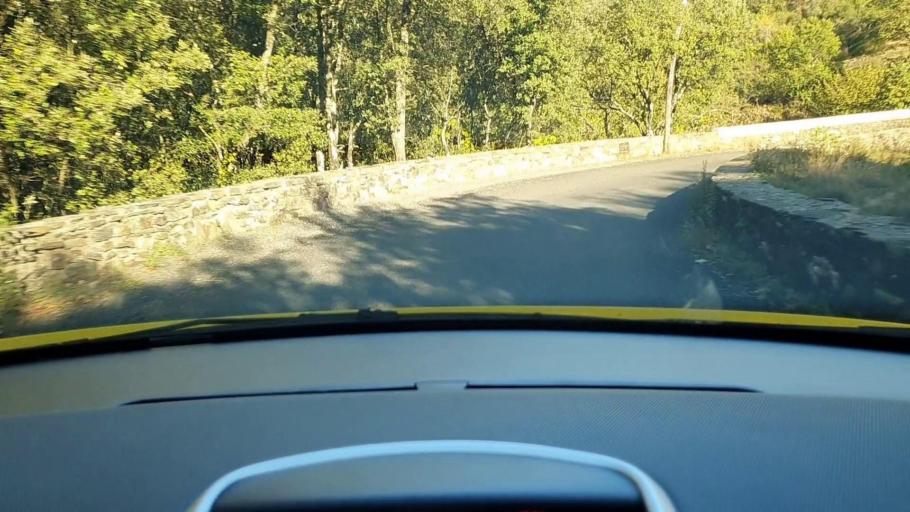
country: FR
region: Languedoc-Roussillon
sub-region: Departement du Gard
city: Sumene
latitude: 44.0197
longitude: 3.7254
